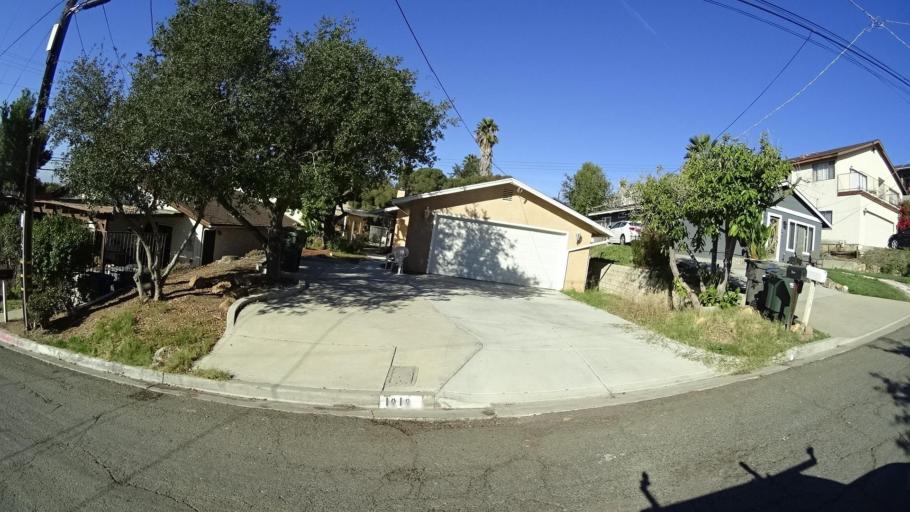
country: US
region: California
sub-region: San Diego County
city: La Presa
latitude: 32.7151
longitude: -116.9933
